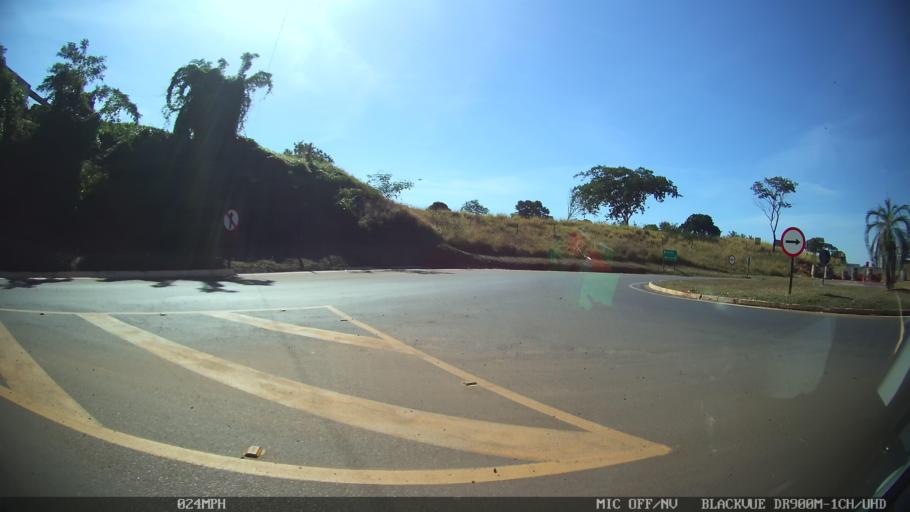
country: BR
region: Sao Paulo
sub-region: Barretos
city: Barretos
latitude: -20.5813
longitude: -48.5801
